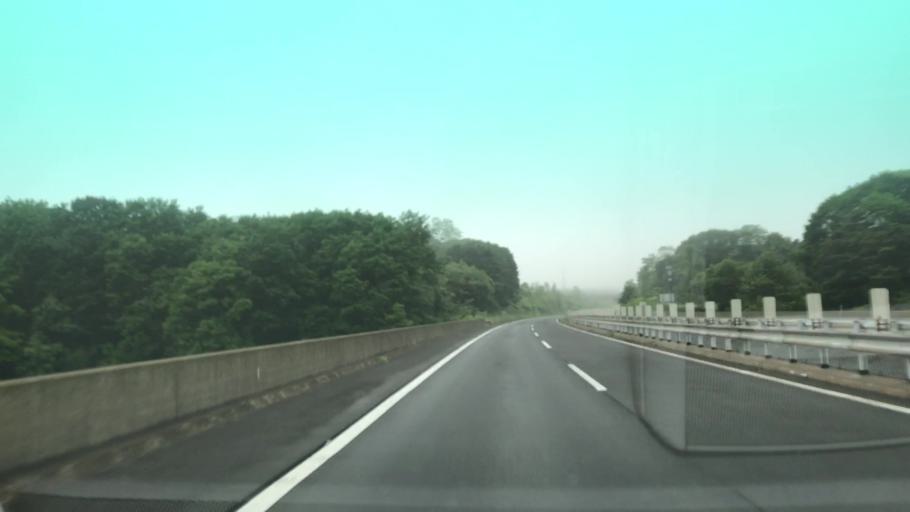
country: JP
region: Hokkaido
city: Muroran
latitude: 42.4495
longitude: 141.1586
